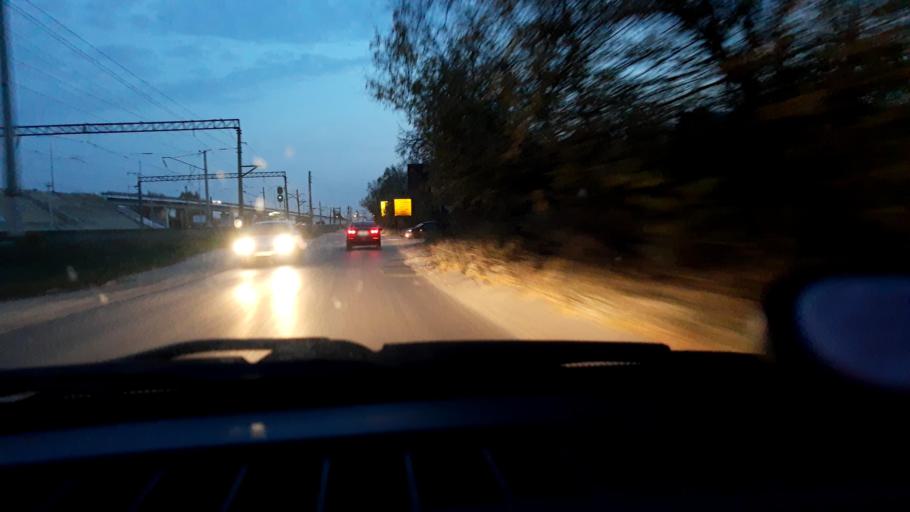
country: RU
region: Nizjnij Novgorod
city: Neklyudovo
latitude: 56.4025
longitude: 43.9815
